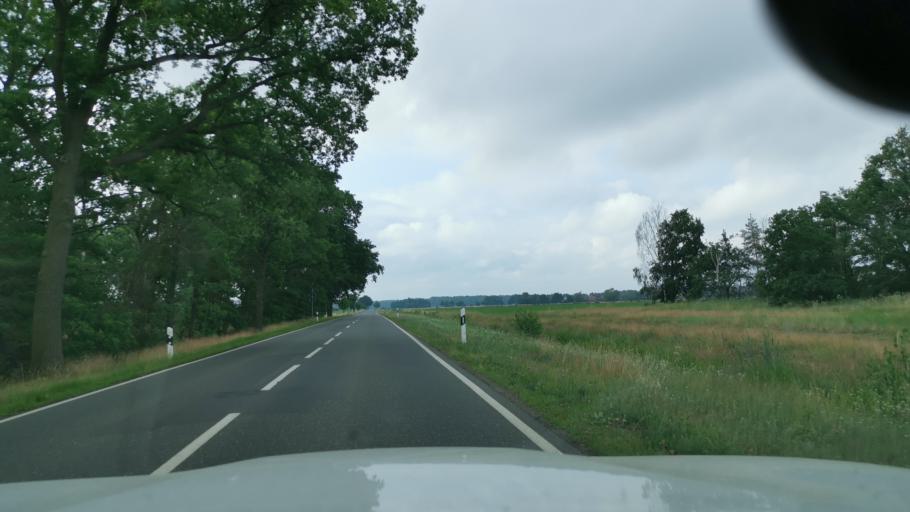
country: DE
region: Saxony-Anhalt
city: Annaburg
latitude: 51.7725
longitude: 13.0268
